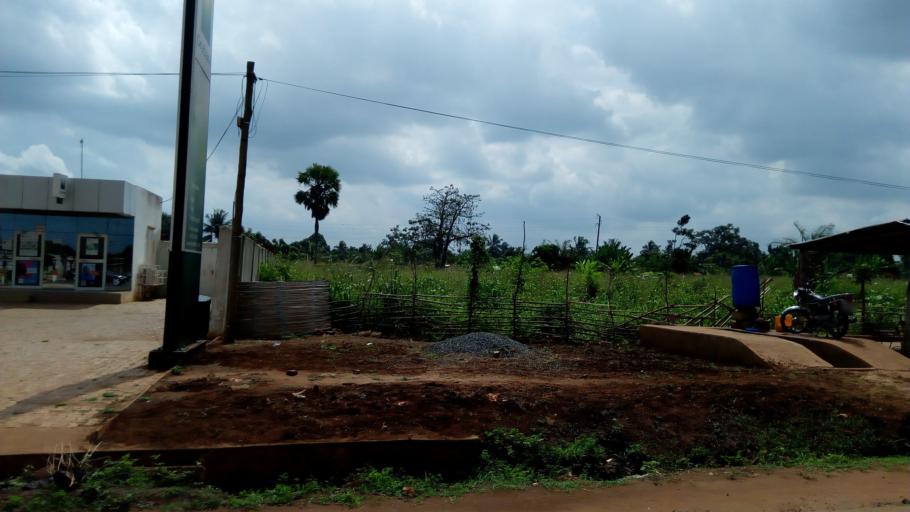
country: TG
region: Maritime
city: Tsevie
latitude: 6.4343
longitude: 1.2120
